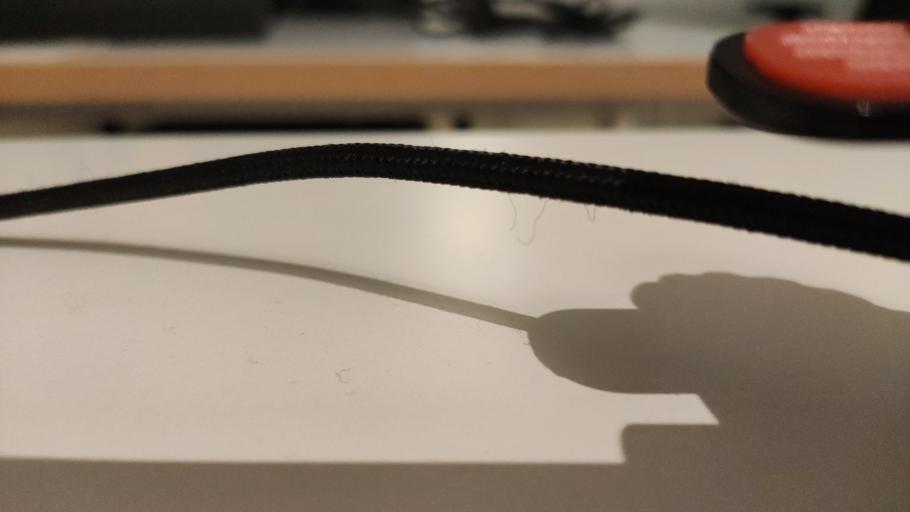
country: RU
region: Moskovskaya
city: Novosin'kovo
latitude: 56.3795
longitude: 37.3256
